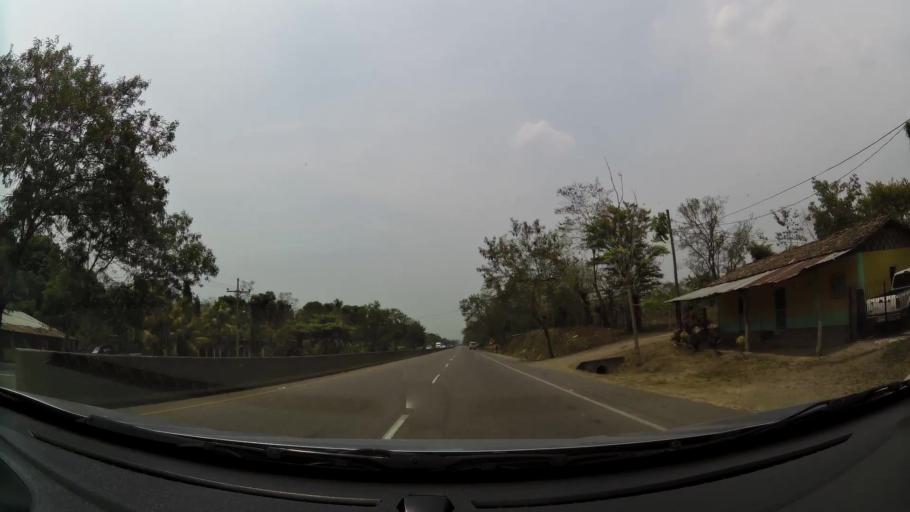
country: HN
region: Cortes
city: Oropendolas
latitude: 15.0506
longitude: -87.9286
